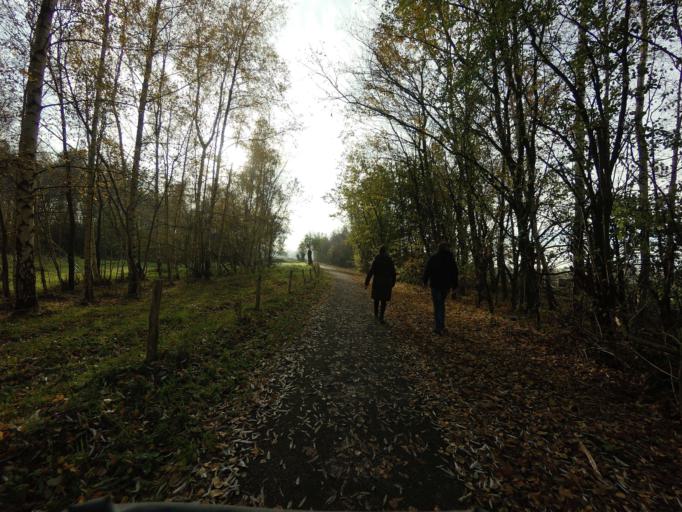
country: NL
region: North Brabant
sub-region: Gemeente Breda
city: Breda
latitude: 51.5097
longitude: 4.7843
